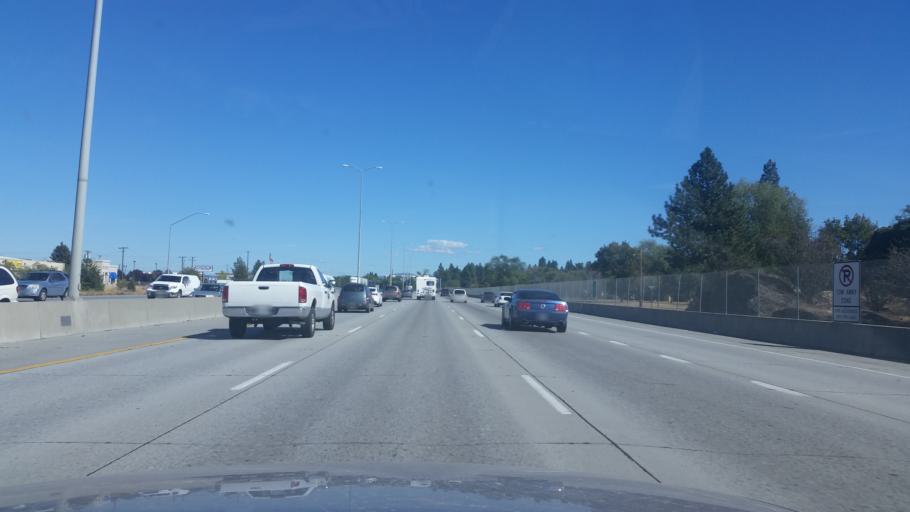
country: US
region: Washington
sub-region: Spokane County
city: Millwood
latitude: 47.6537
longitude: -117.3342
